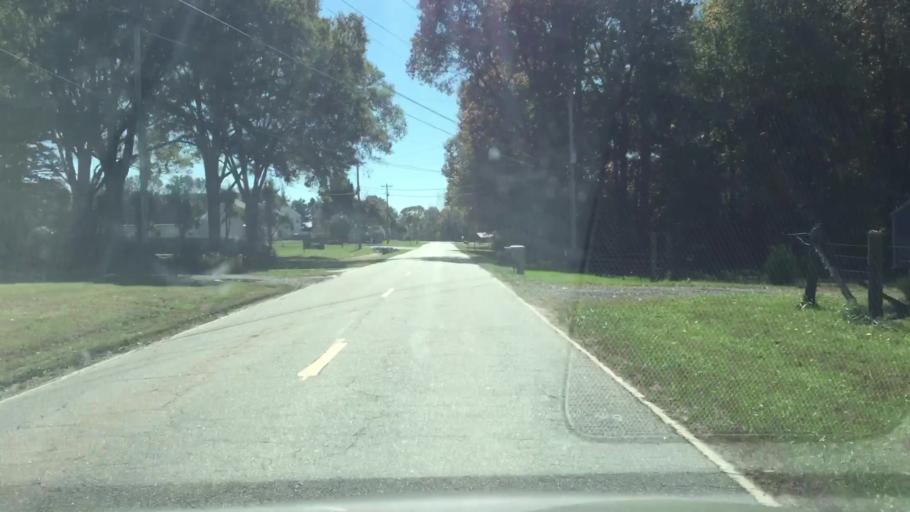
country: US
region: North Carolina
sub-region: Iredell County
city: Mooresville
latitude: 35.5436
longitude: -80.7890
